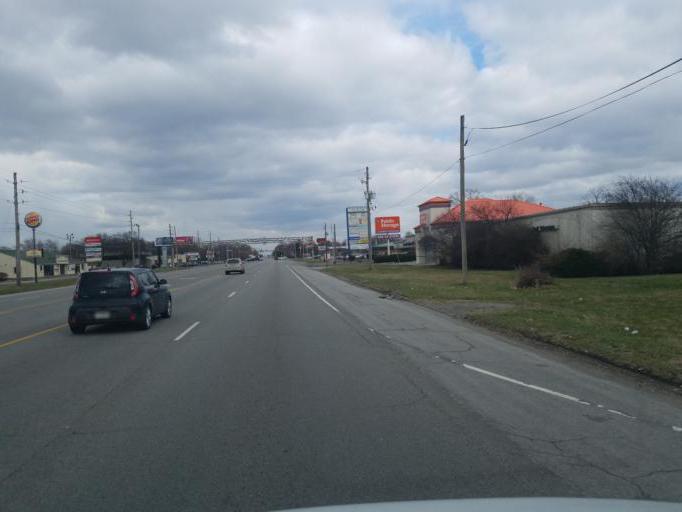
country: US
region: Indiana
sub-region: Marion County
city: Speedway
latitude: 39.7641
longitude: -86.2924
